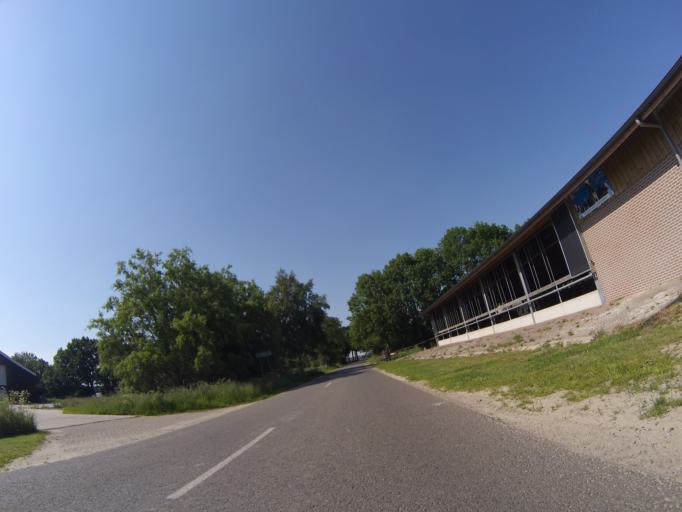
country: NL
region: Drenthe
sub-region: Gemeente Coevorden
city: Dalen
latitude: 52.7169
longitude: 6.8009
